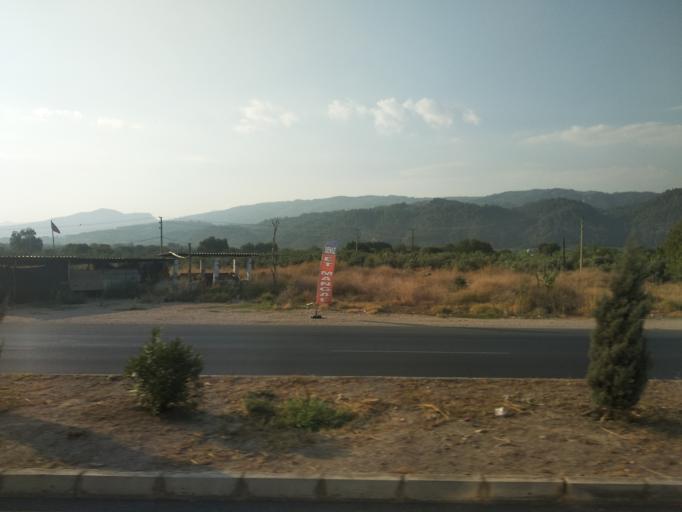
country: TR
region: Manisa
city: Ahmetli
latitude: 38.5032
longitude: 27.8769
